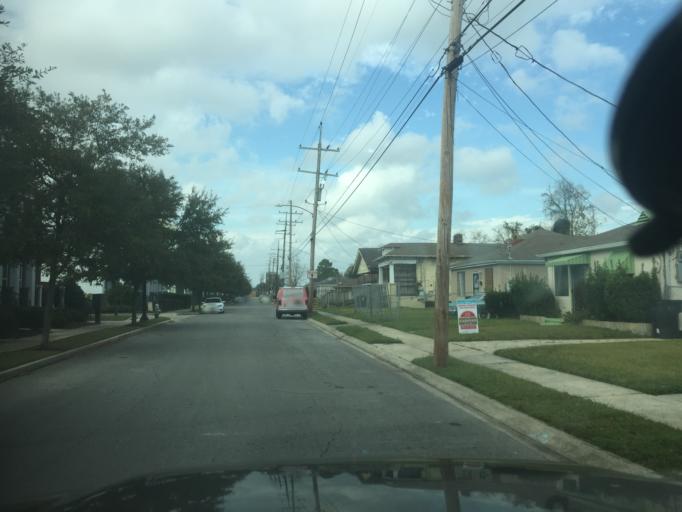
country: US
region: Louisiana
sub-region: Orleans Parish
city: New Orleans
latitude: 29.9963
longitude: -90.0748
